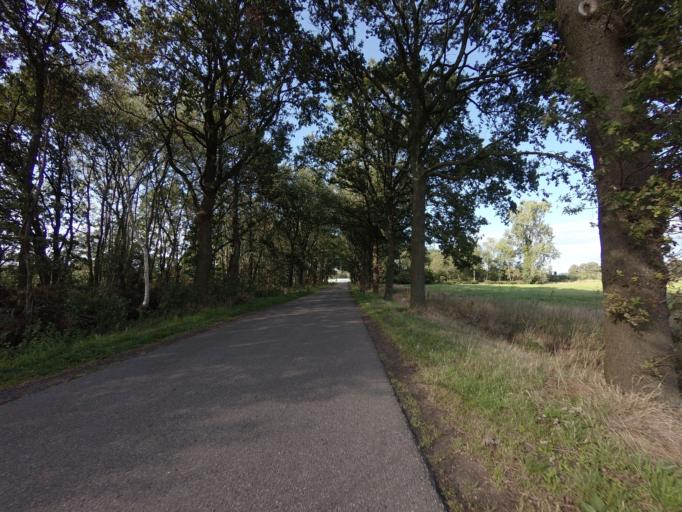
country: NL
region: Friesland
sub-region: Gemeente Heerenveen
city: Jubbega
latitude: 52.9973
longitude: 6.2306
